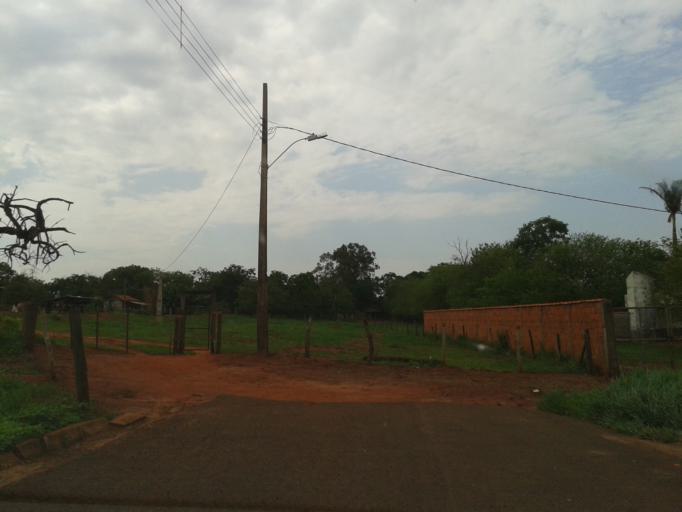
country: BR
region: Minas Gerais
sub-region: Ituiutaba
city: Ituiutaba
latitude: -18.9776
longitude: -49.4420
